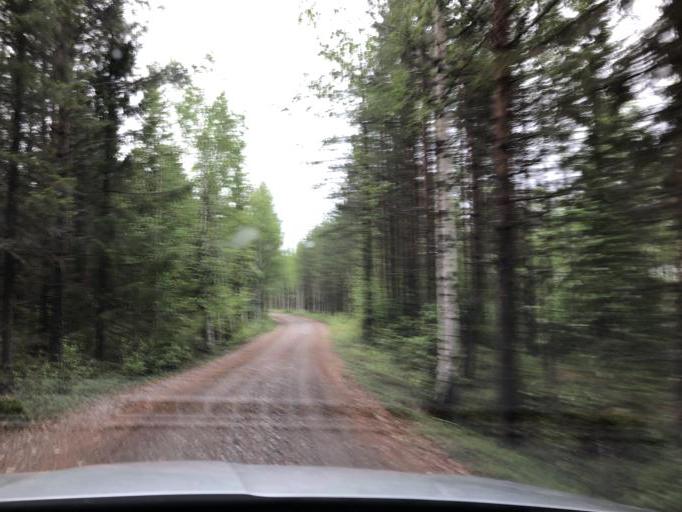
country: SE
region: Norrbotten
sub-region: Pitea Kommun
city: Roknas
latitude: 65.3965
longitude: 21.2648
